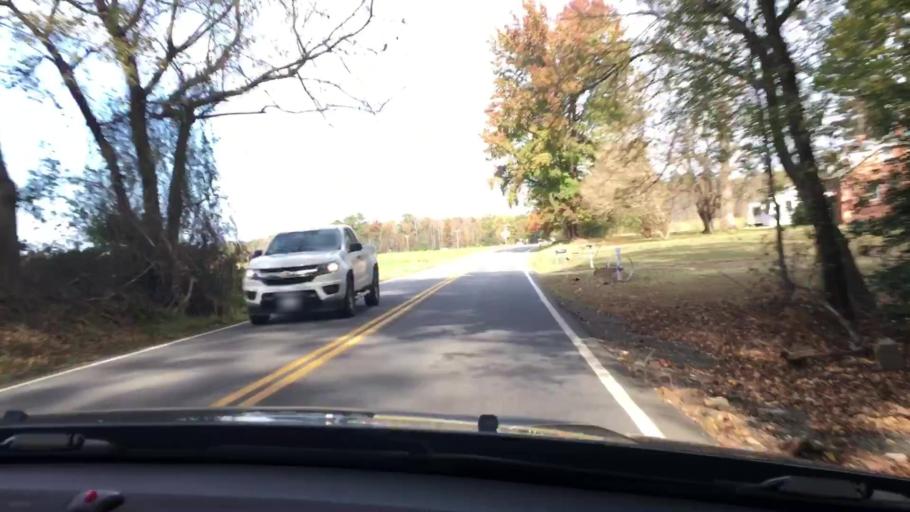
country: US
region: Virginia
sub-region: King William County
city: West Point
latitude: 37.5086
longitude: -76.8213
